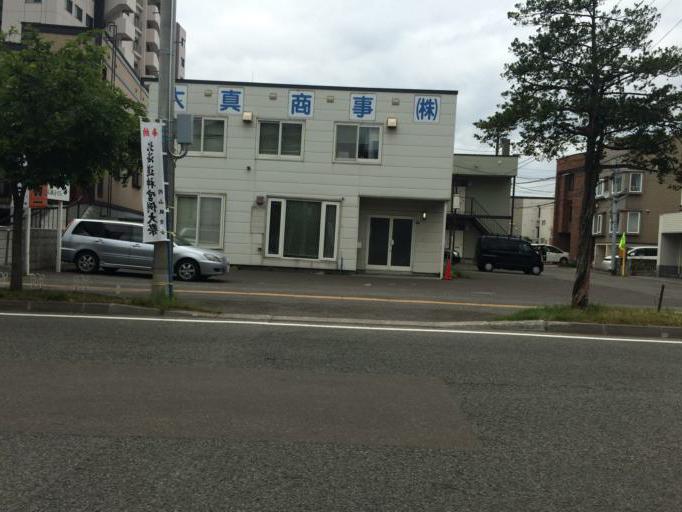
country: JP
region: Hokkaido
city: Sapporo
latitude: 43.0578
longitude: 141.3161
